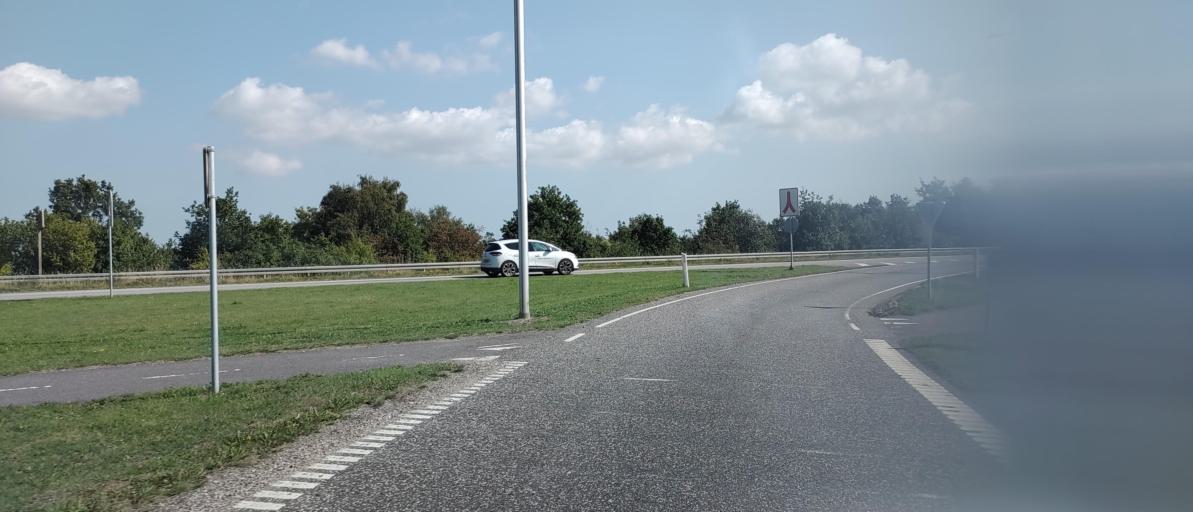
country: DK
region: Zealand
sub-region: Guldborgsund Kommune
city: Norre Alslev
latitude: 54.8634
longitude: 11.8521
